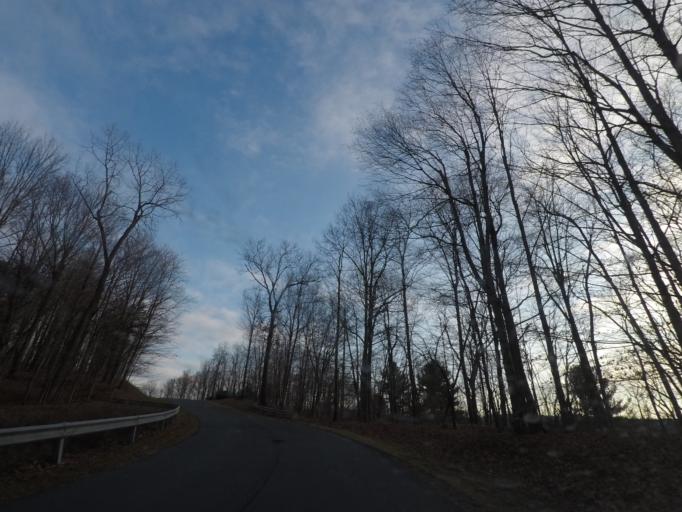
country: US
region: New York
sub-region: Rensselaer County
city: Wynantskill
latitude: 42.7229
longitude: -73.6436
